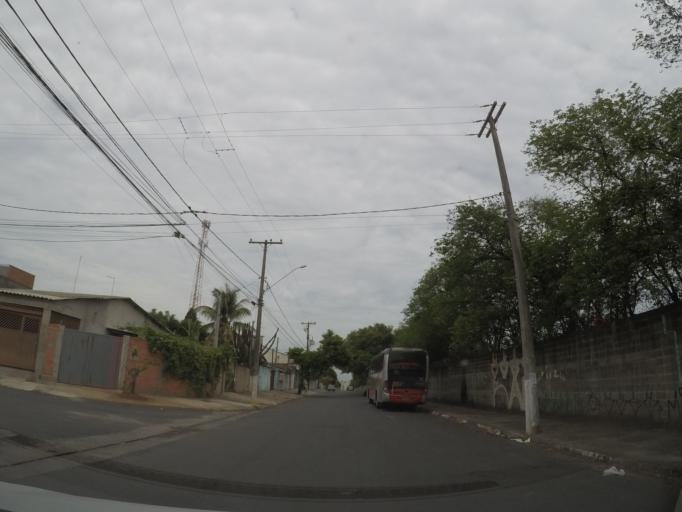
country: BR
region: Sao Paulo
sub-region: Hortolandia
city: Hortolandia
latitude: -22.8355
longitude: -47.1964
